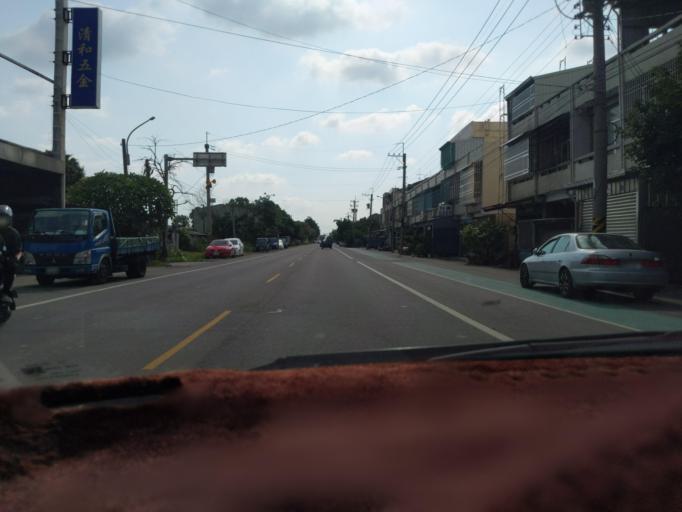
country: TW
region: Taiwan
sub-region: Yunlin
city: Douliu
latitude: 23.7966
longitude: 120.4280
